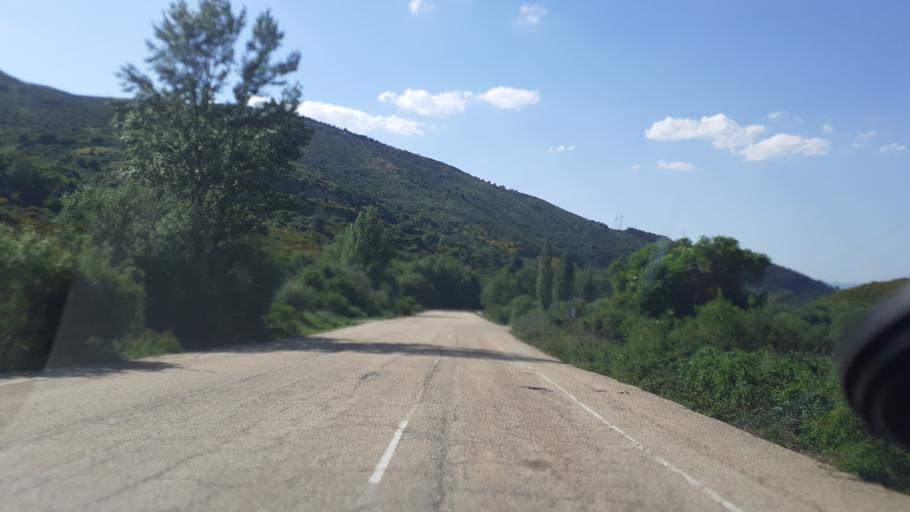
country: ES
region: Madrid
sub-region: Provincia de Madrid
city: Somosierra
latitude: 41.1471
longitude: -3.5800
